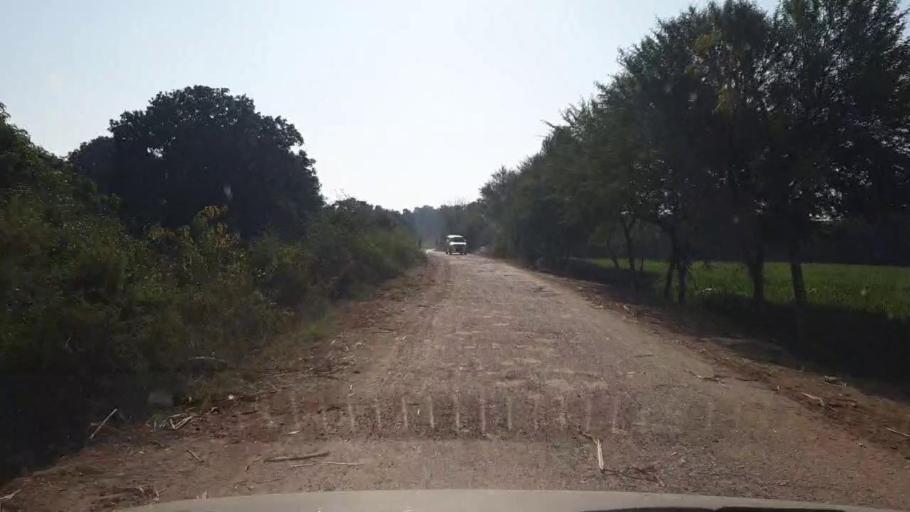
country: PK
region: Sindh
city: Tando Jam
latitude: 25.4297
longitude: 68.6055
